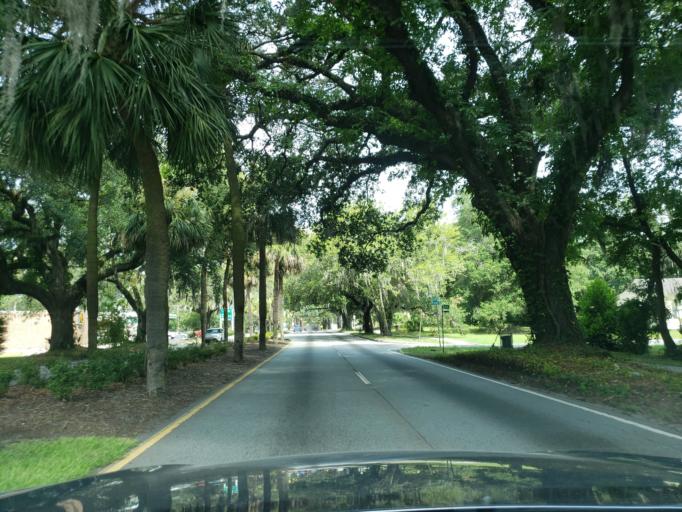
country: US
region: Georgia
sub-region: Chatham County
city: Thunderbolt
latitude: 32.0454
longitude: -81.0752
